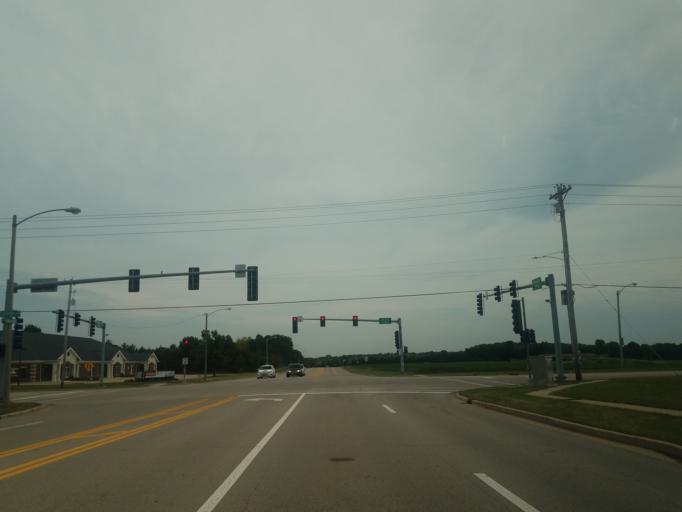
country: US
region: Illinois
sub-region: McLean County
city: Normal
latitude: 40.5108
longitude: -88.9419
